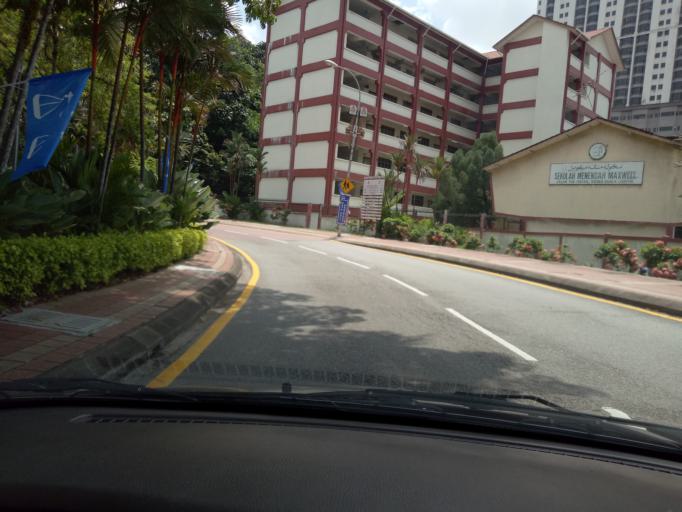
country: MY
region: Kuala Lumpur
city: Kuala Lumpur
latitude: 3.1701
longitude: 101.6909
